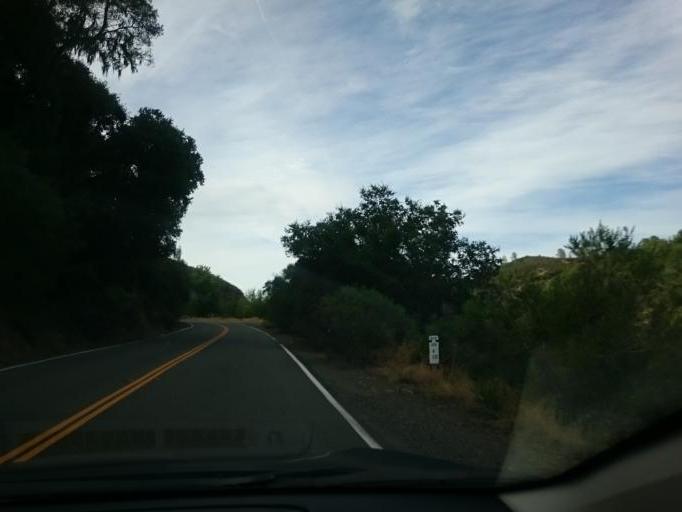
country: US
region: California
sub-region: Napa County
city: Yountville
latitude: 38.4877
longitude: -122.2980
